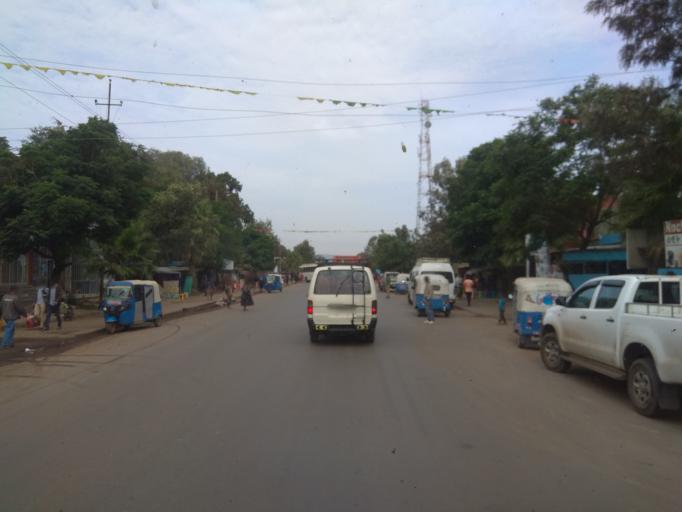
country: ET
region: Oromiya
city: Hagere Hiywet
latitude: 8.9821
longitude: 37.8529
